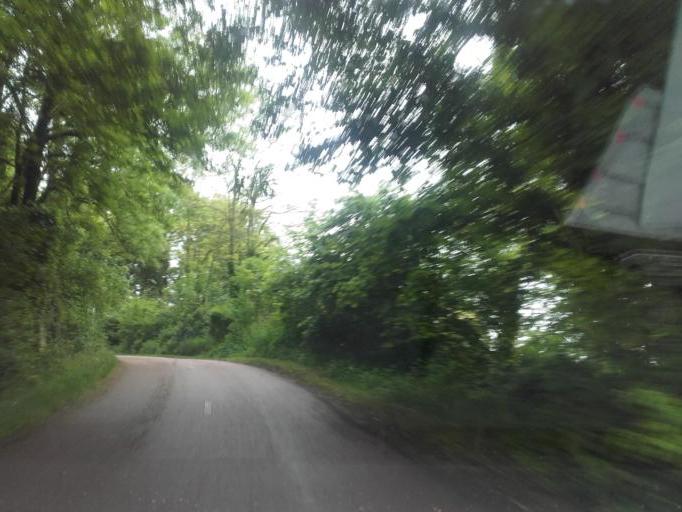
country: FR
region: Bourgogne
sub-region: Departement de la Cote-d'Or
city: Nolay
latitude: 46.9908
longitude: 4.6929
